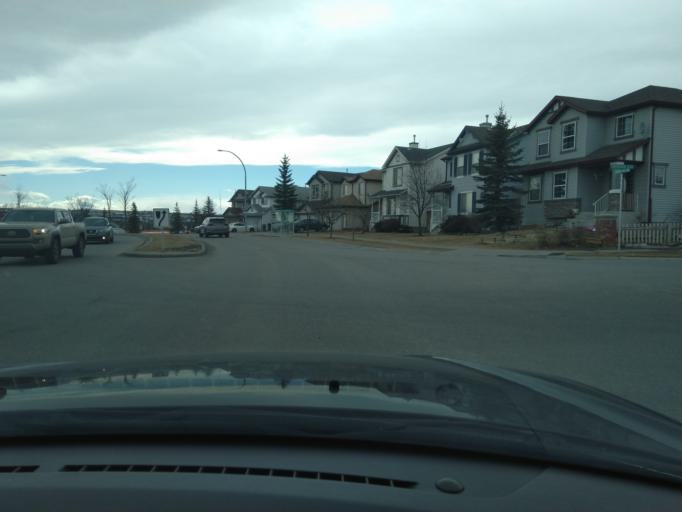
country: CA
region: Alberta
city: Calgary
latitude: 51.1689
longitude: -114.0620
